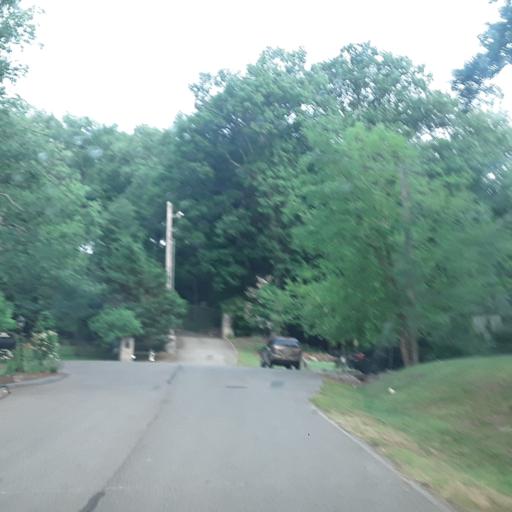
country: US
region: Tennessee
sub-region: Williamson County
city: Brentwood
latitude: 36.0567
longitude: -86.7803
